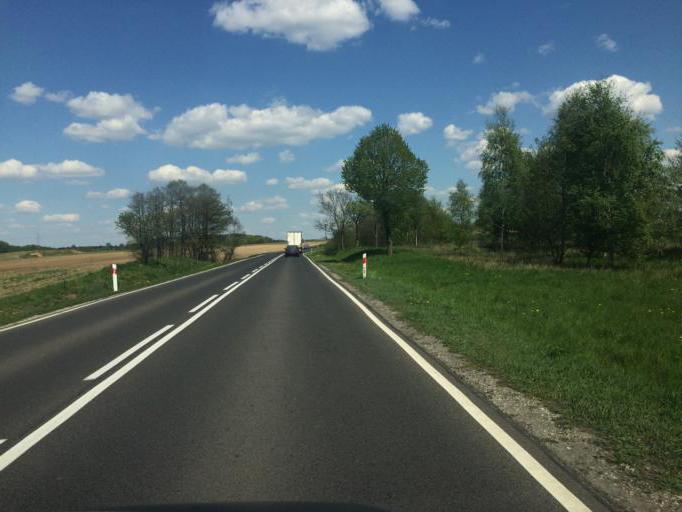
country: PL
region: Warmian-Masurian Voivodeship
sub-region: Powiat olsztynski
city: Gietrzwald
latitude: 53.7379
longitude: 20.2102
